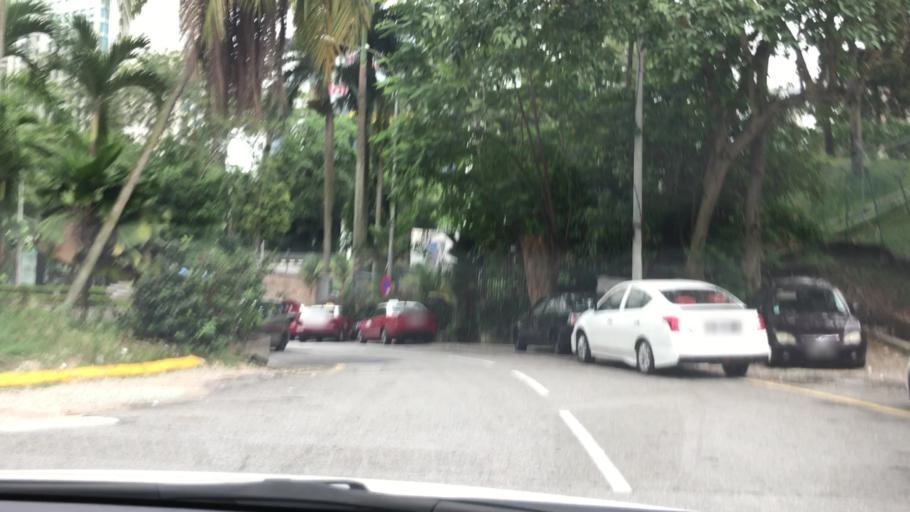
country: MY
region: Kuala Lumpur
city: Kuala Lumpur
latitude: 3.1529
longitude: 101.7050
